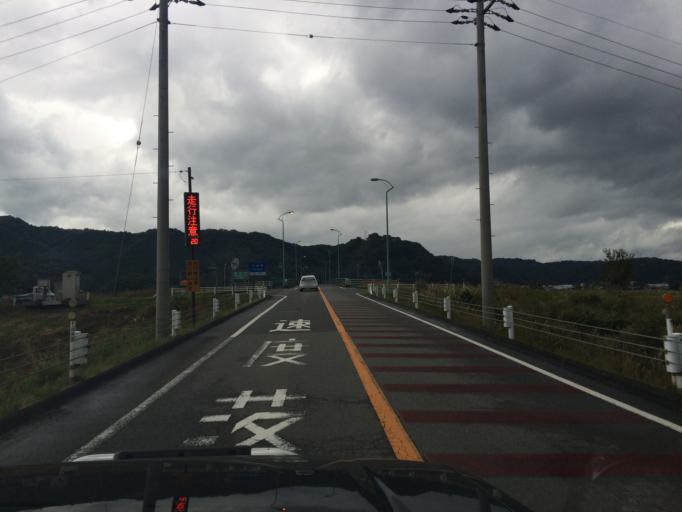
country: JP
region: Hyogo
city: Toyooka
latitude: 35.4527
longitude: 134.7788
